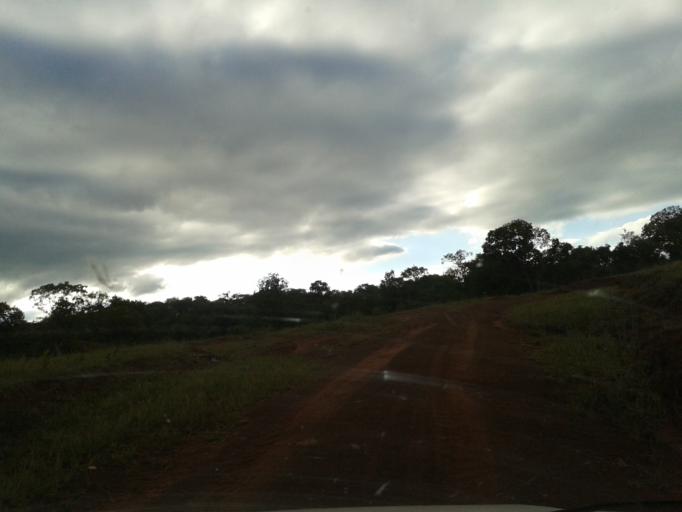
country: BR
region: Minas Gerais
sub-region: Campina Verde
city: Campina Verde
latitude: -19.4858
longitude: -49.6523
